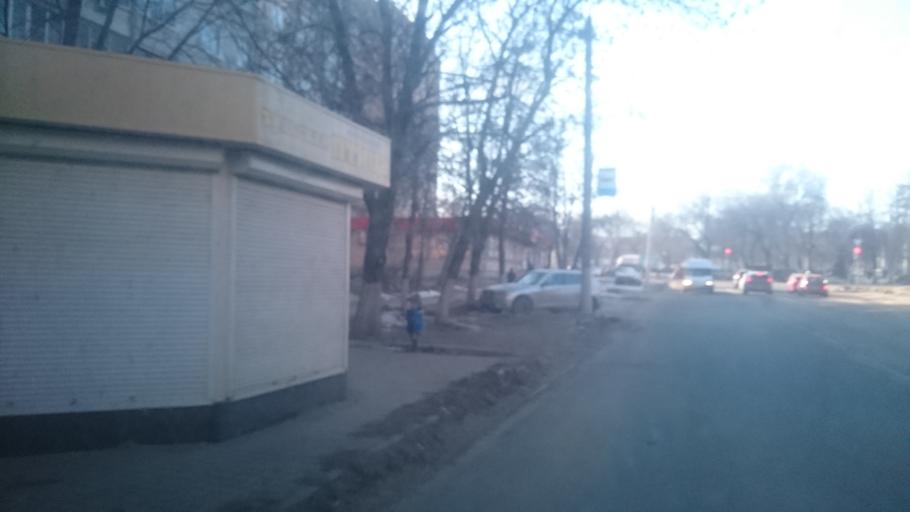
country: RU
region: Tula
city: Tula
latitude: 54.1778
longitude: 37.6317
